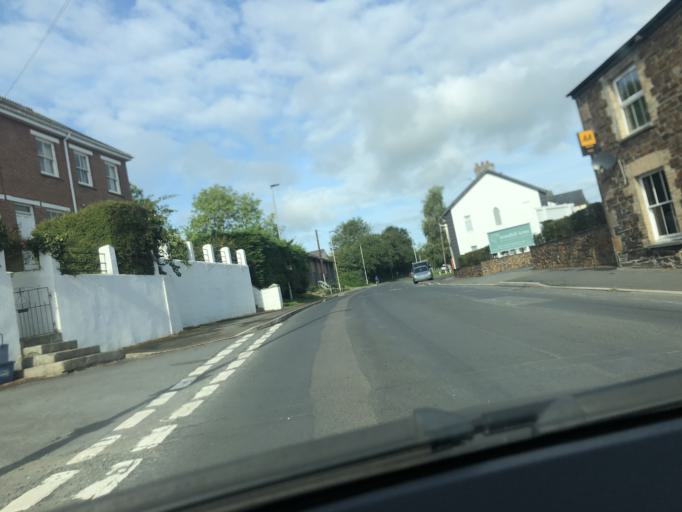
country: GB
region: England
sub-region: Cornwall
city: Launceston
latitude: 50.6432
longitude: -4.2846
